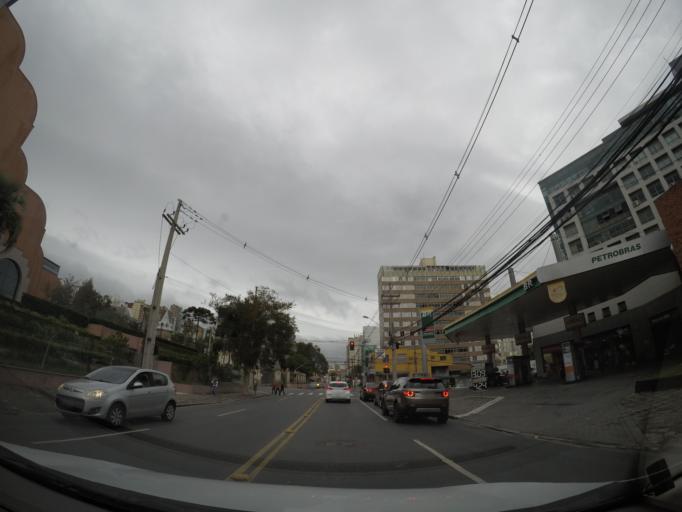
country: BR
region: Parana
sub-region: Curitiba
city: Curitiba
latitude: -25.4415
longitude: -49.2852
